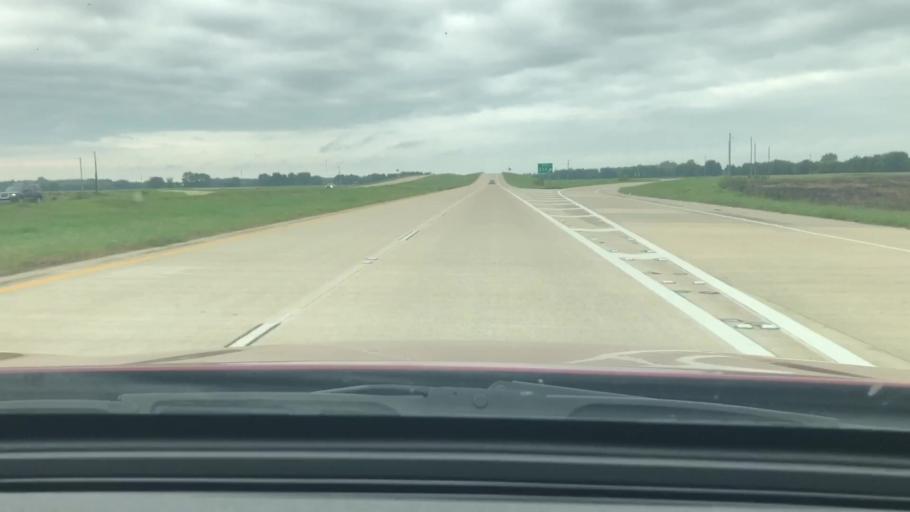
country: US
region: Louisiana
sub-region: Caddo Parish
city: Oil City
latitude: 32.7078
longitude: -93.8644
